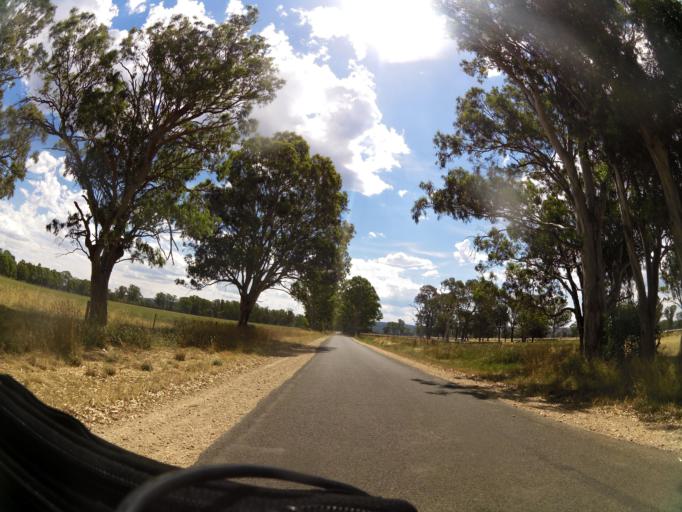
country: AU
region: Victoria
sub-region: Wellington
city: Heyfield
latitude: -37.9833
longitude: 146.7174
